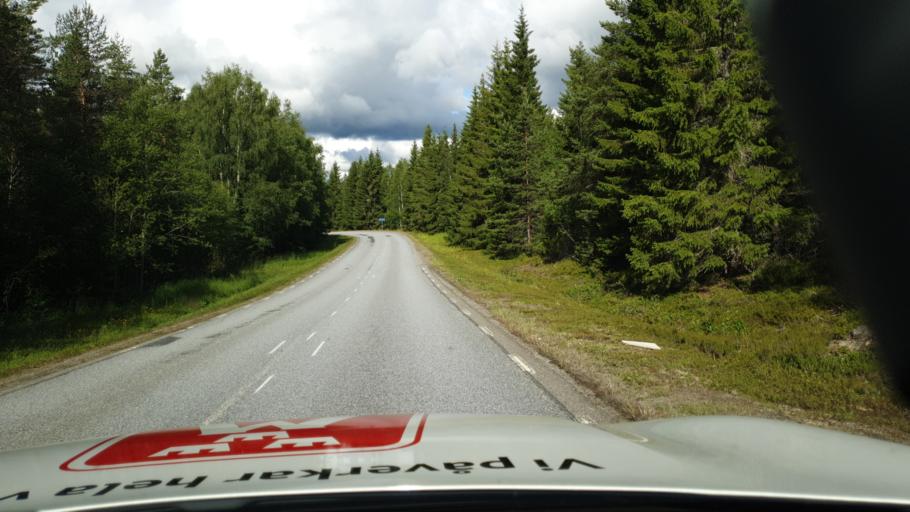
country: SE
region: Vaesterbotten
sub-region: Umea Kommun
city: Roback
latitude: 63.6773
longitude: 20.0777
